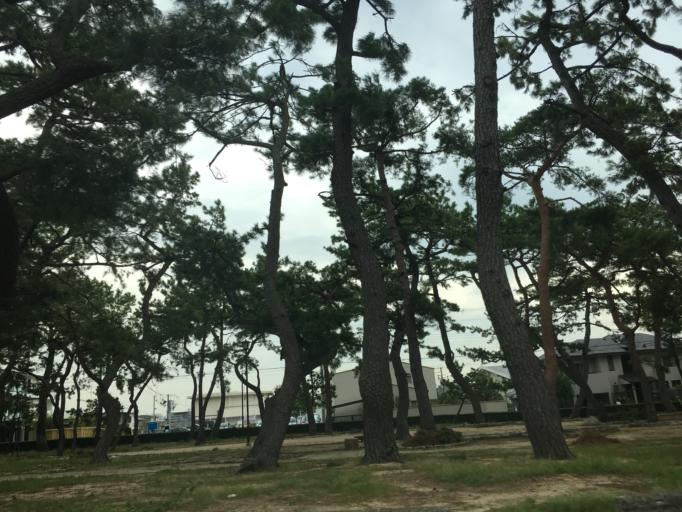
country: JP
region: Hyogo
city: Ashiya
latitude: 34.7238
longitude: 135.3046
